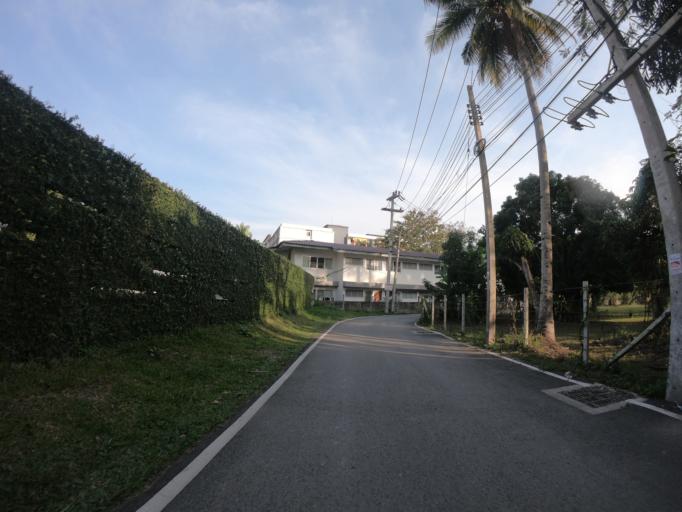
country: TH
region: Chiang Mai
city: Chiang Mai
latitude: 18.8179
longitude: 98.9563
